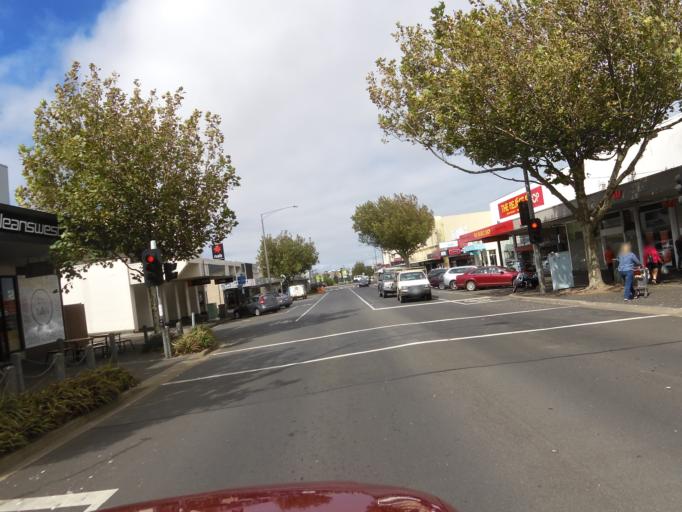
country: AU
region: Victoria
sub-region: Warrnambool
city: Warrnambool
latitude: -38.3831
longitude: 142.4824
